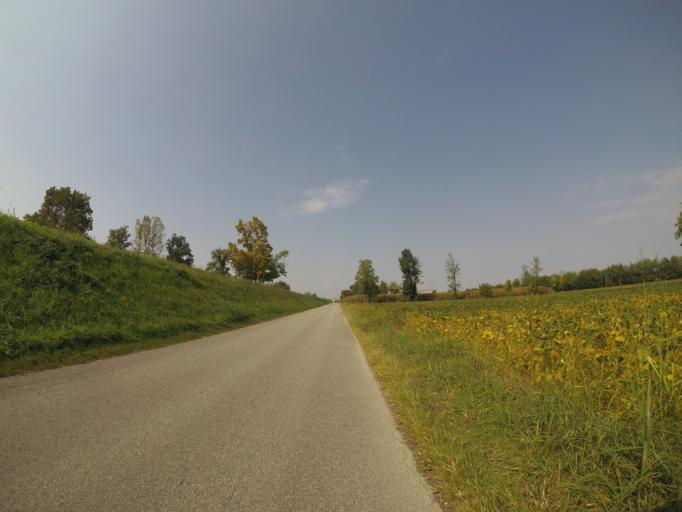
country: IT
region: Friuli Venezia Giulia
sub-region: Provincia di Udine
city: Camino al Tagliamento
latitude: 45.9036
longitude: 12.9369
